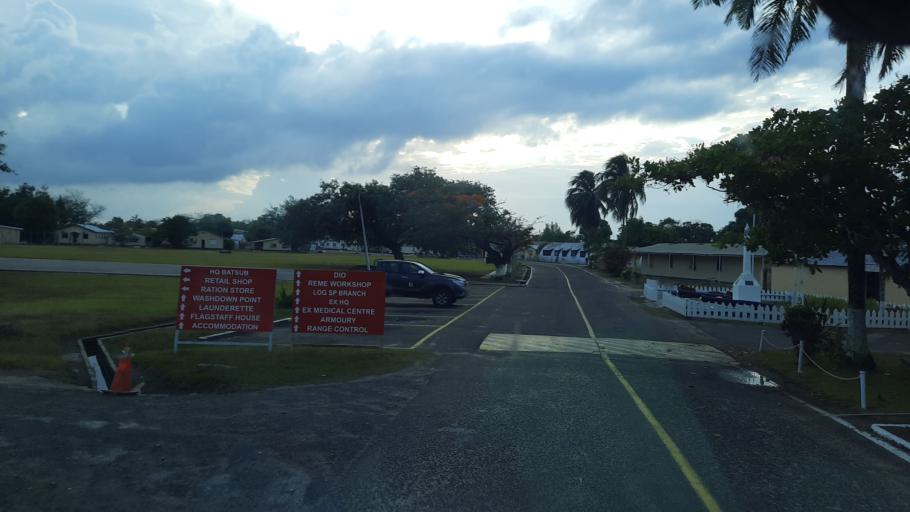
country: BZ
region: Belize
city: Belize City
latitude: 17.5432
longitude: -88.3039
